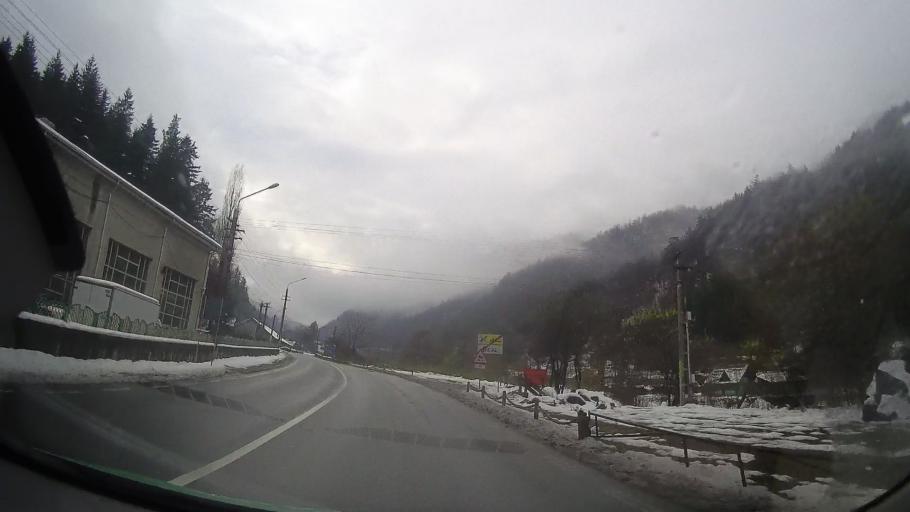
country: RO
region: Neamt
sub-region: Comuna Bicaz
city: Bicaz
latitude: 46.9009
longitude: 26.0689
